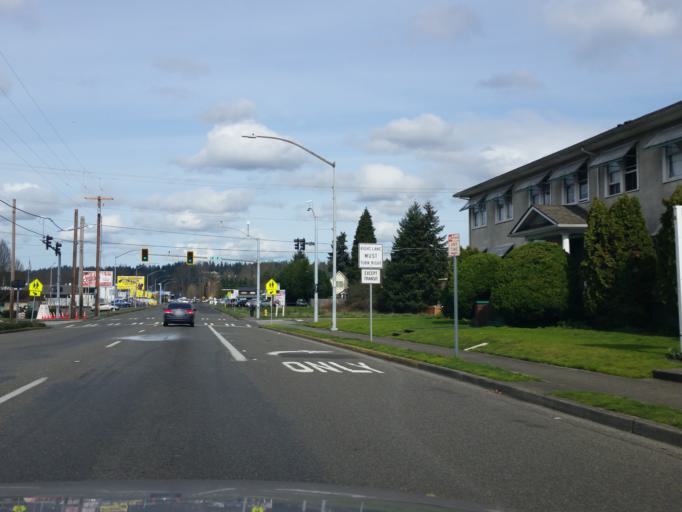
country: US
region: Washington
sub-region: Pierce County
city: Puyallup
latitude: 47.1949
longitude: -122.2921
